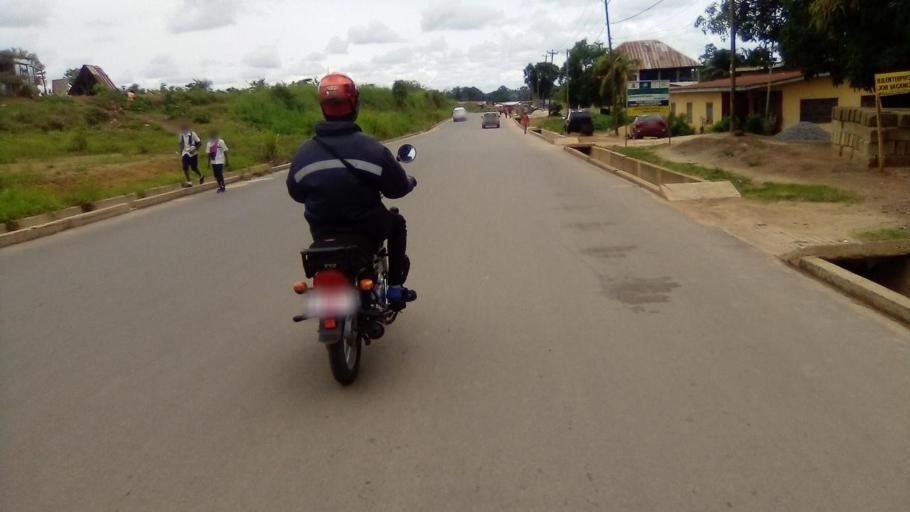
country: SL
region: Southern Province
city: Bo
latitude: 7.9483
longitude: -11.7575
